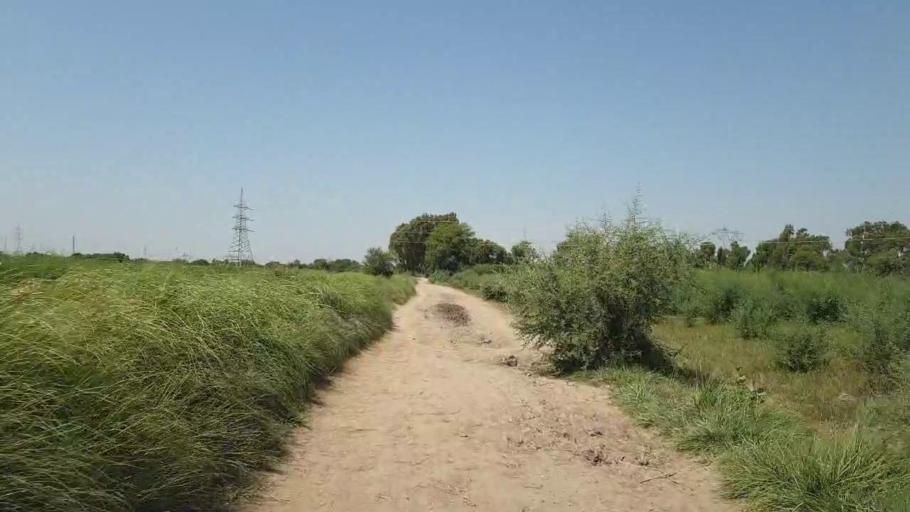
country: PK
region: Sindh
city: Hyderabad
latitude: 25.4759
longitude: 68.4159
